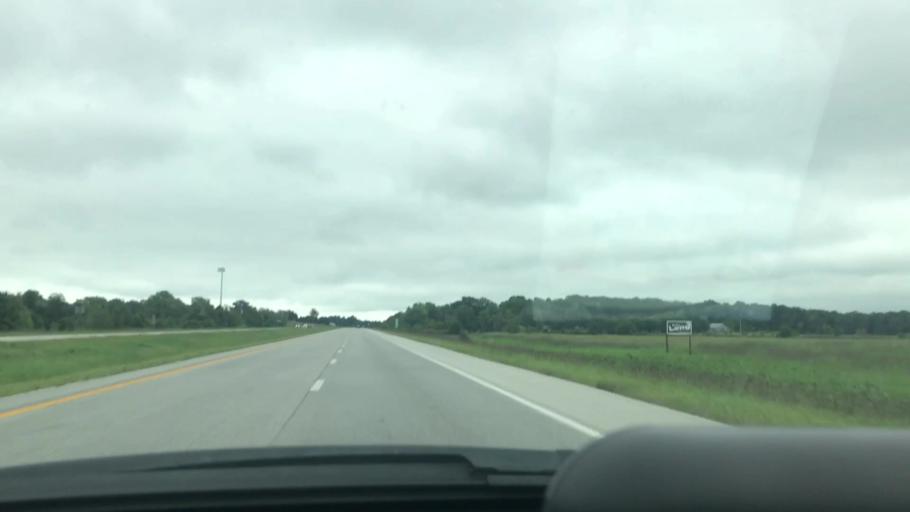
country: US
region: Missouri
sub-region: Greene County
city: Strafford
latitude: 37.2772
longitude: -93.2085
